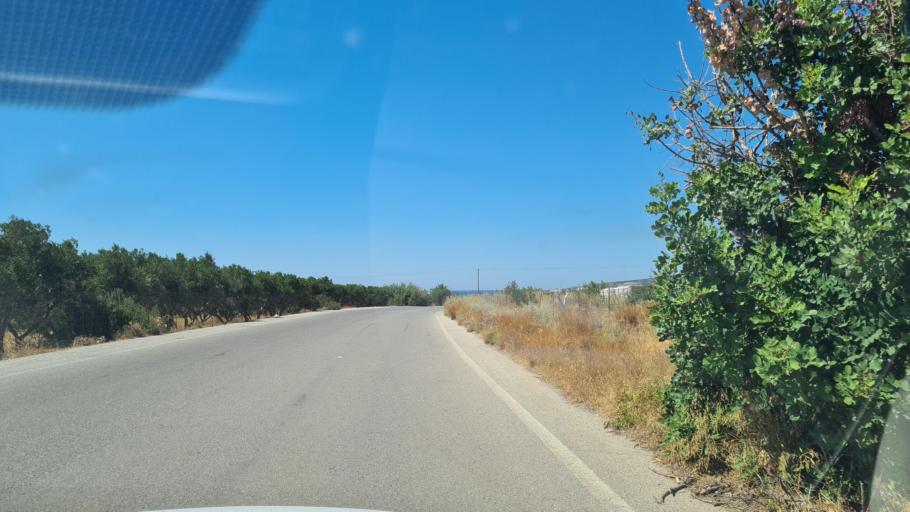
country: GR
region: Crete
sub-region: Nomos Chanias
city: Vryses
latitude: 35.3019
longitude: 23.5379
